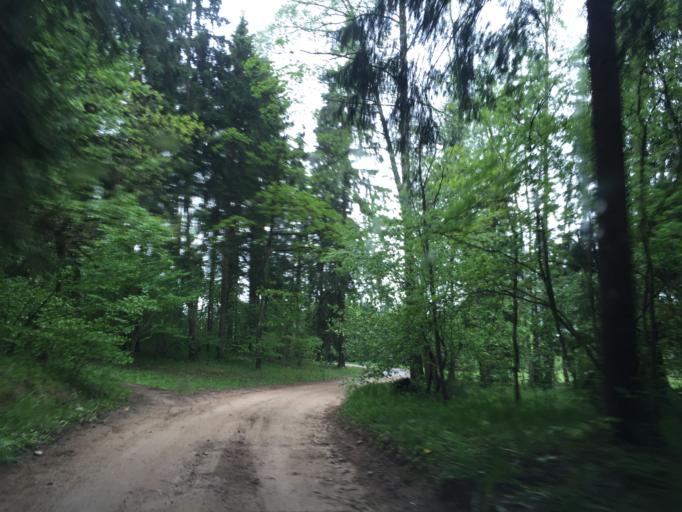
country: LV
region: Kegums
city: Kegums
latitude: 56.7365
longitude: 24.7415
